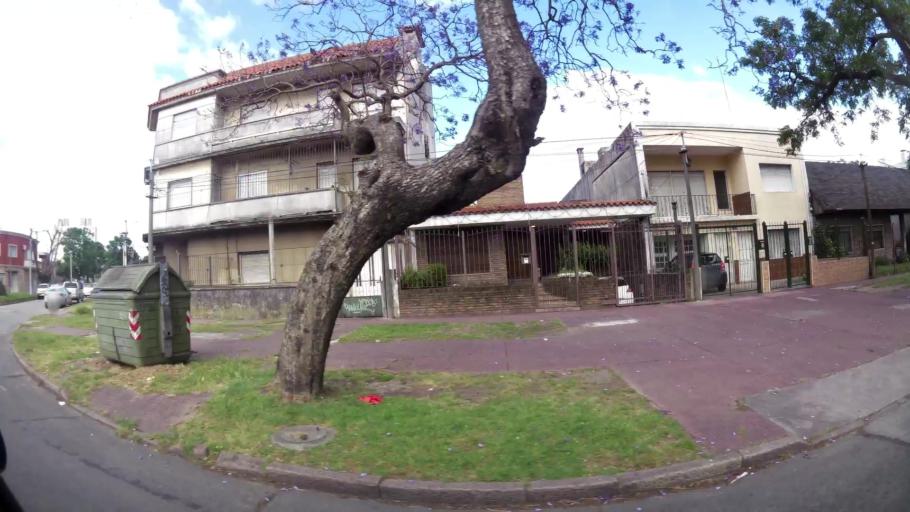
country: UY
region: Montevideo
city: Montevideo
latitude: -34.8781
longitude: -56.1525
